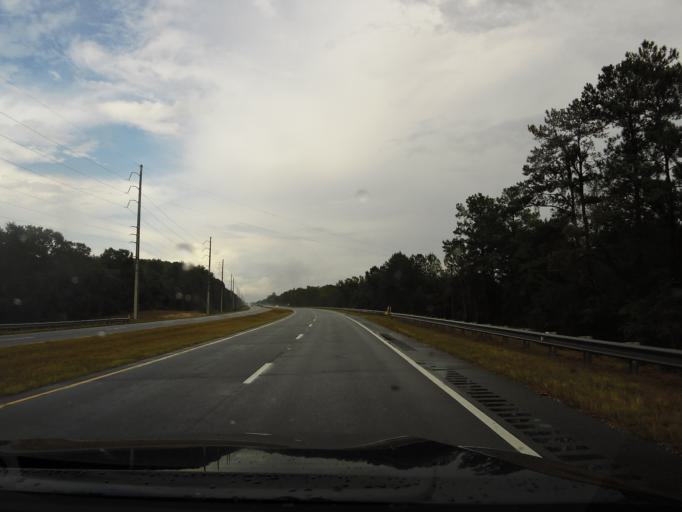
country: US
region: Georgia
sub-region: Long County
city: Ludowici
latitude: 31.6812
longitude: -81.8060
